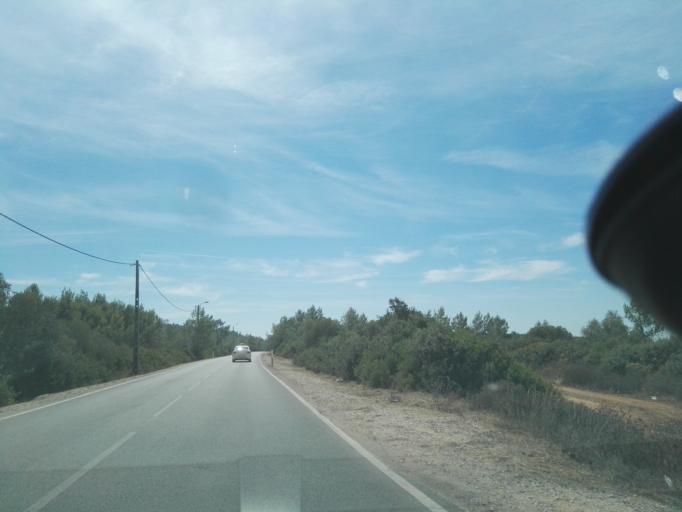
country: PT
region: Setubal
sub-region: Sesimbra
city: Sesimbra
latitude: 38.4534
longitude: -9.0909
